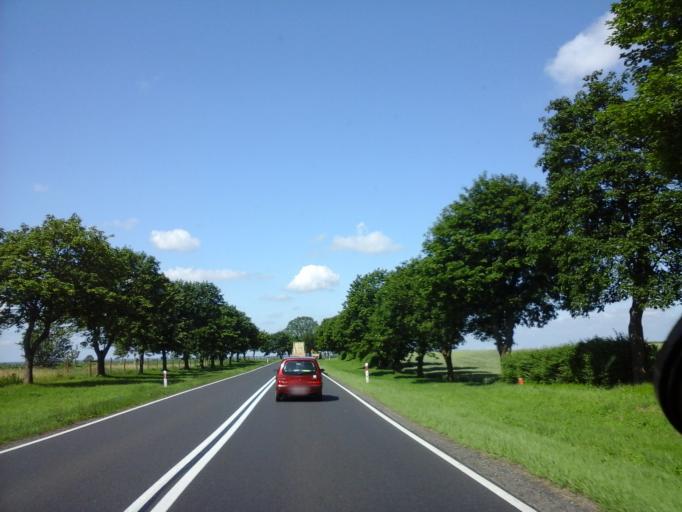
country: PL
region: West Pomeranian Voivodeship
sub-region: Powiat stargardzki
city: Dobrzany
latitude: 53.2726
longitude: 15.4540
